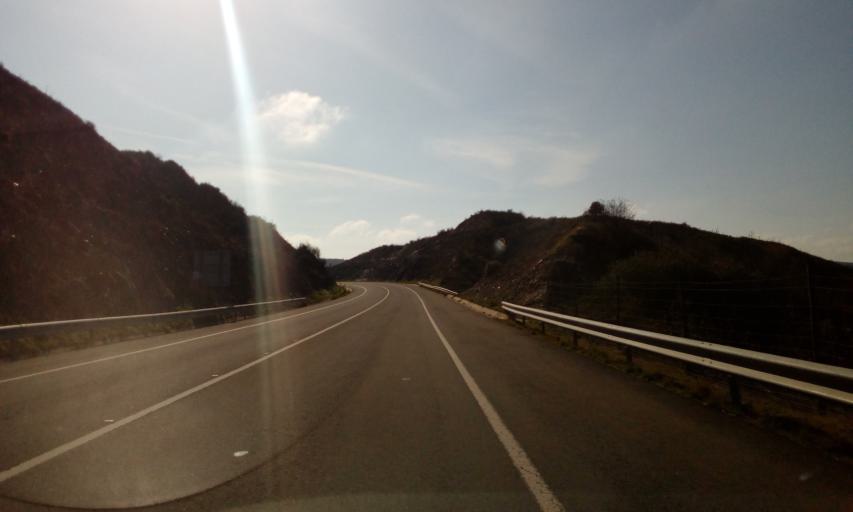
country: PT
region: Faro
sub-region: Alcoutim
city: Alcoutim
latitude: 37.3941
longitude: -7.5271
